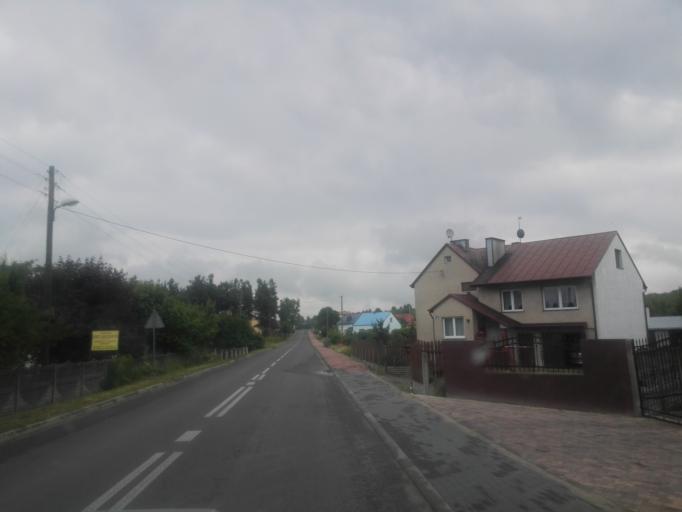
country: PL
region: Silesian Voivodeship
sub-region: Powiat czestochowski
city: Olsztyn
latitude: 50.7210
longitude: 19.3299
